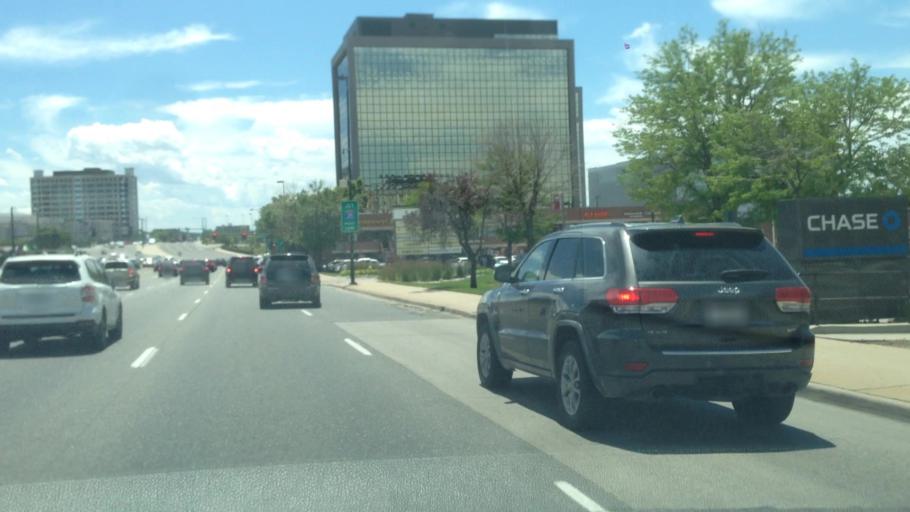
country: US
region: Colorado
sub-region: Arapahoe County
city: Glendale
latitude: 39.6873
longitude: -104.9408
